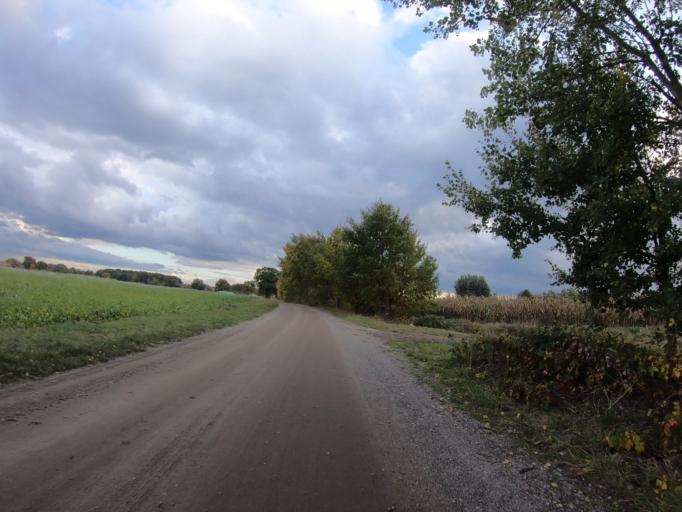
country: DE
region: Lower Saxony
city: Wagenhoff
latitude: 52.5237
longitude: 10.5233
